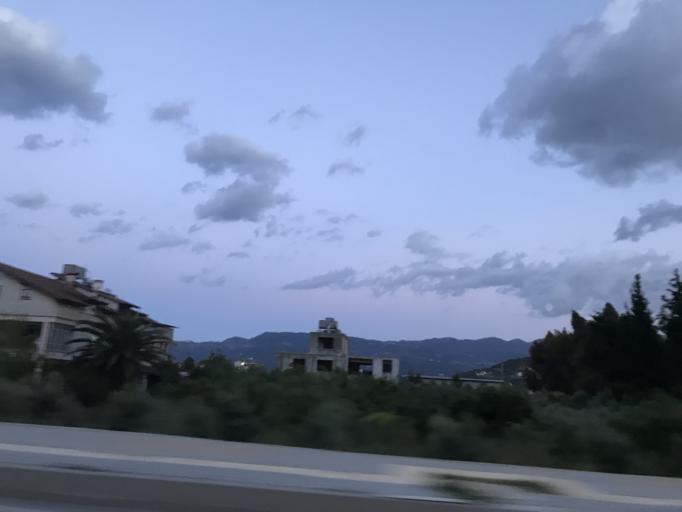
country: TR
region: Hatay
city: Uzunbag
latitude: 36.1364
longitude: 36.0431
